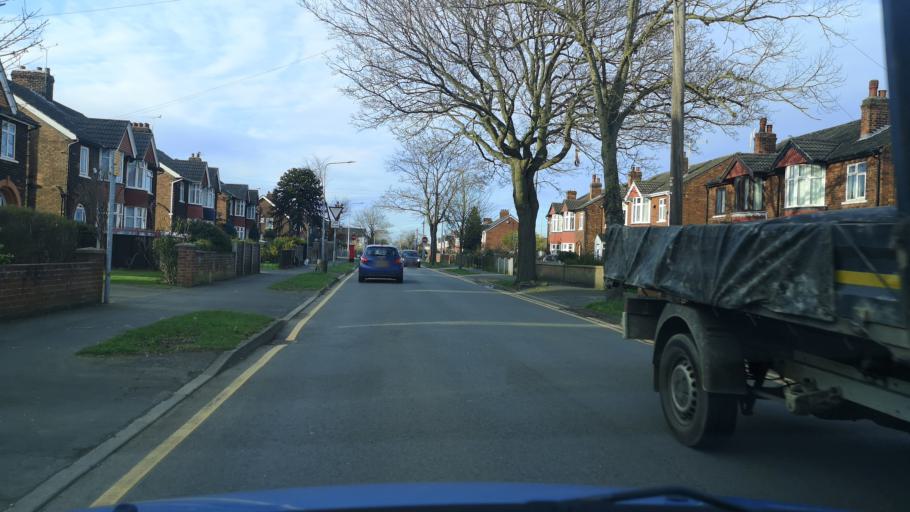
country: GB
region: England
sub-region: North Lincolnshire
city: Scunthorpe
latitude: 53.5872
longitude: -0.6610
